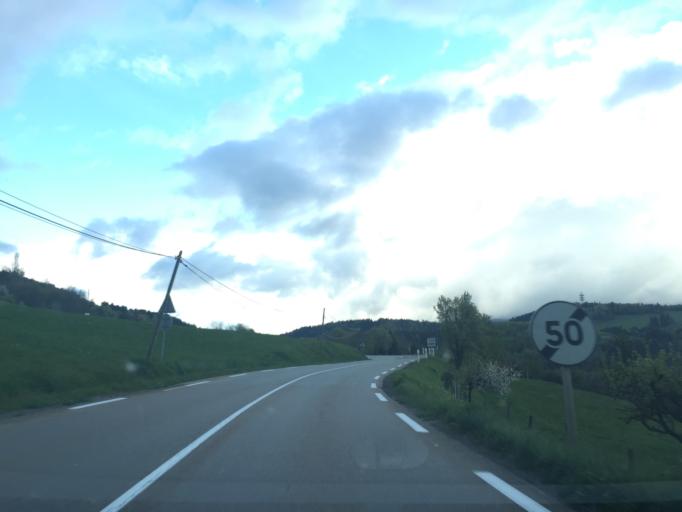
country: FR
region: Rhone-Alpes
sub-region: Departement de l'Isere
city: La Motte-Saint-Martin
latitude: 44.9009
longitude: 5.6162
